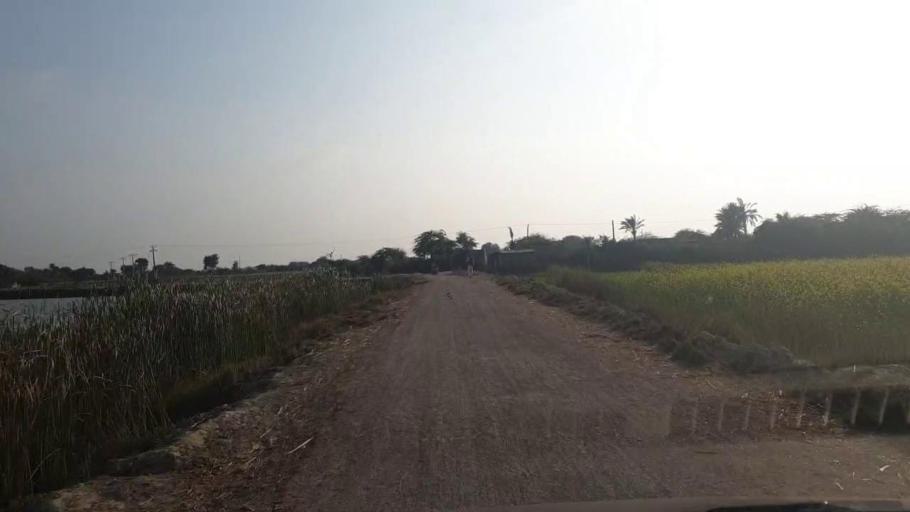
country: PK
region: Sindh
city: Shahdadpur
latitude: 25.8772
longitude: 68.7300
